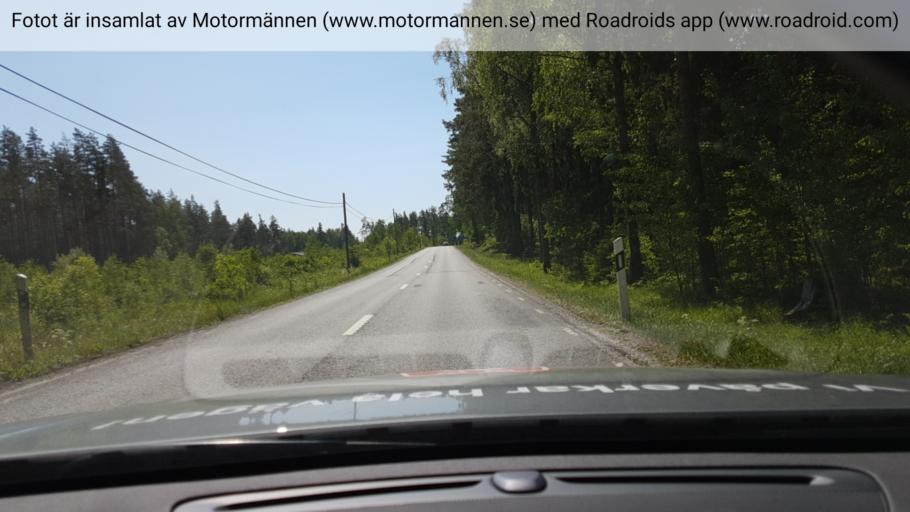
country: SE
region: Stockholm
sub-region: Norrtalje Kommun
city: Rimbo
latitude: 59.7786
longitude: 18.4361
